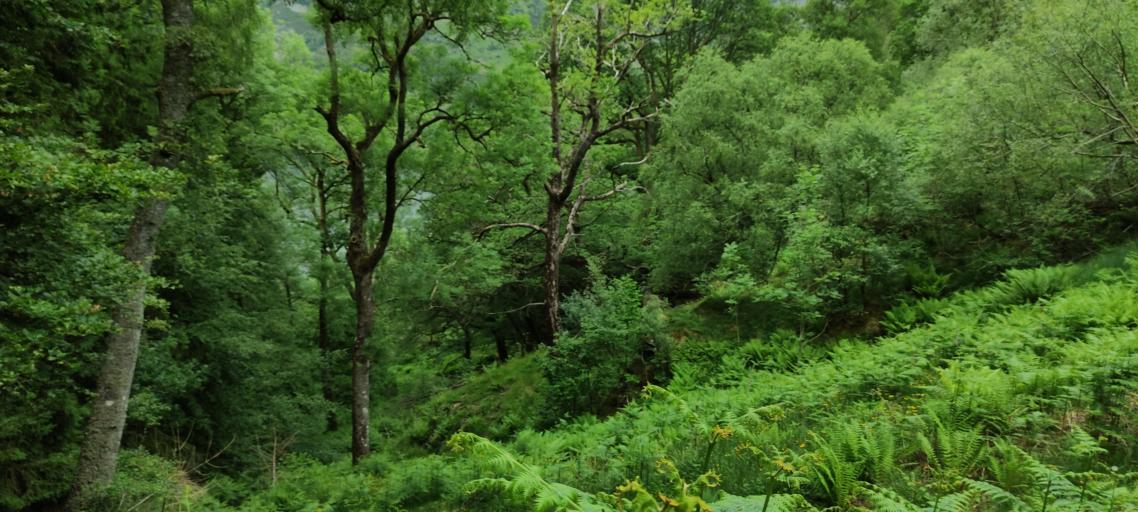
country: GB
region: England
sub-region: Cumbria
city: Ambleside
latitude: 54.5526
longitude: -2.9519
